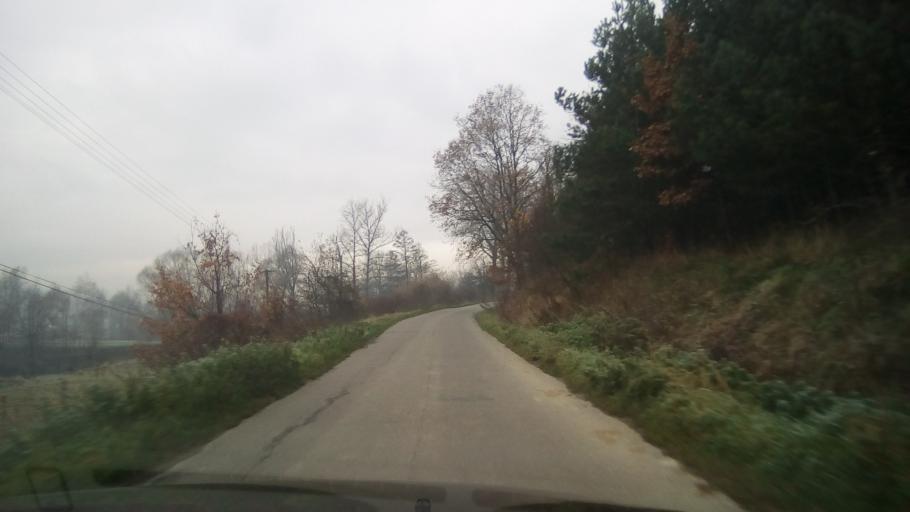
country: PL
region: Subcarpathian Voivodeship
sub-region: Powiat strzyzowski
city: Strzyzow
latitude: 49.8529
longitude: 21.8048
